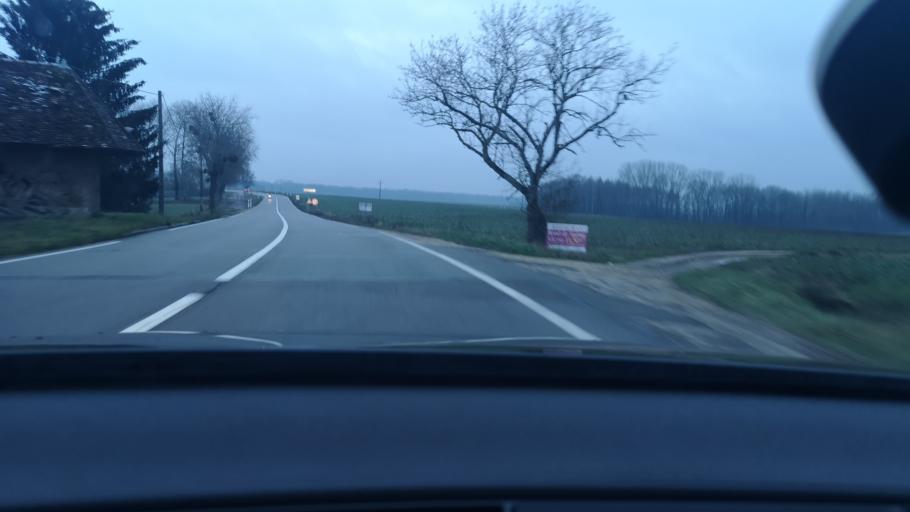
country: FR
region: Bourgogne
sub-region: Departement de la Cote-d'Or
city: Seurre
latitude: 47.0626
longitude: 5.0947
